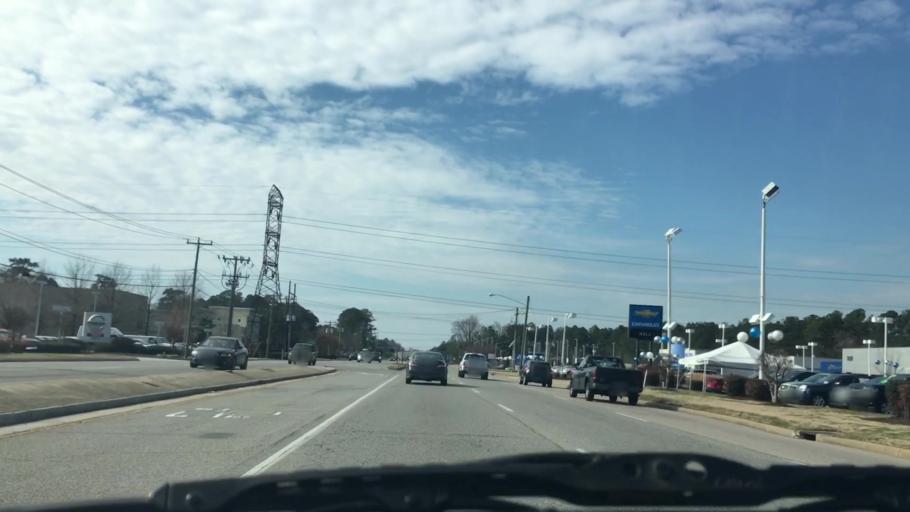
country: US
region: Virginia
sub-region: City of Portsmouth
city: Portsmouth Heights
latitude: 36.8655
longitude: -76.4172
